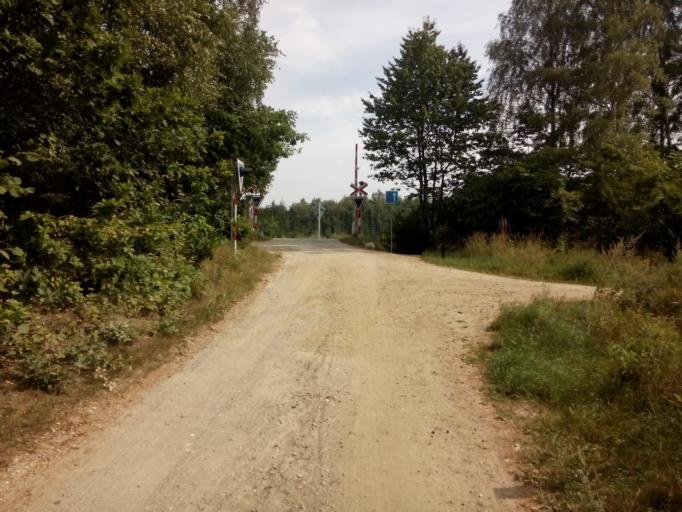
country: DK
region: Central Jutland
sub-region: Skanderborg Kommune
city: Ry
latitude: 56.0966
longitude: 9.7371
